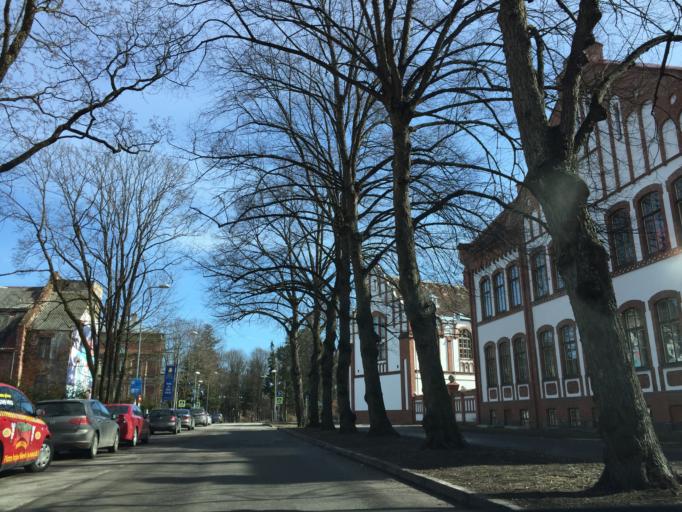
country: EE
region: Paernumaa
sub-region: Paernu linn
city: Parnu
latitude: 58.3832
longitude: 24.5000
